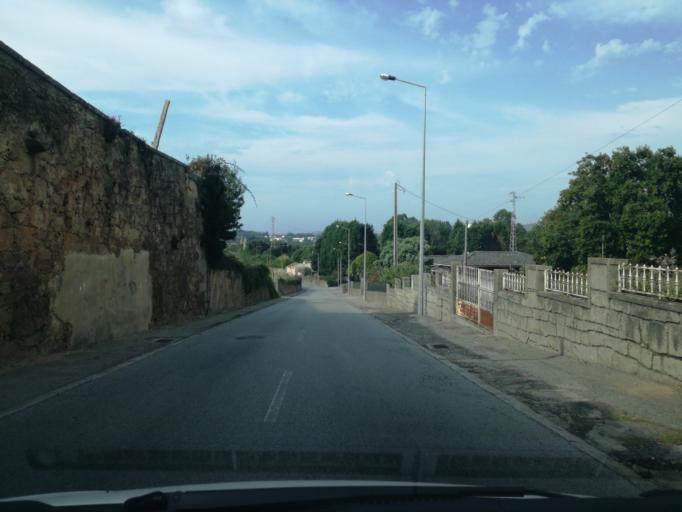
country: PT
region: Porto
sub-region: Vila Nova de Gaia
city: Arcozelo
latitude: 41.0532
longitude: -8.6266
